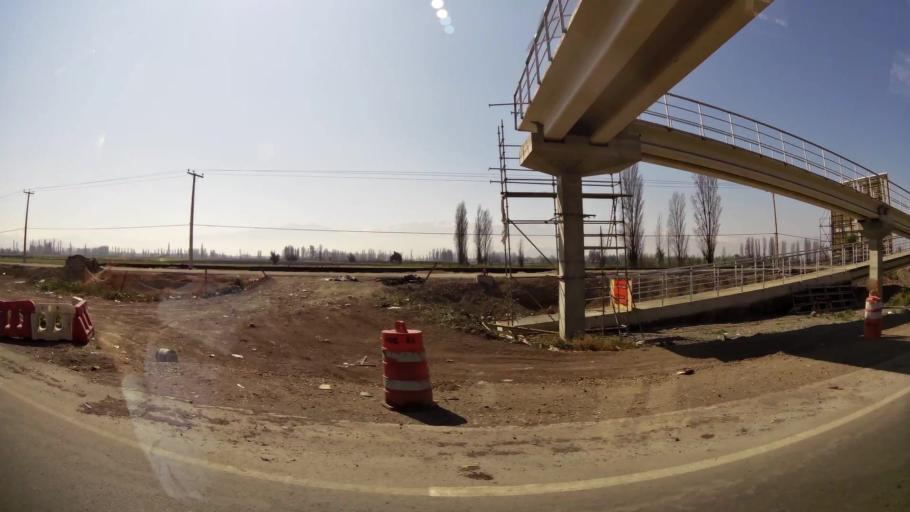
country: CL
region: Santiago Metropolitan
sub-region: Provincia de Chacabuco
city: Chicureo Abajo
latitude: -33.2631
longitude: -70.7463
